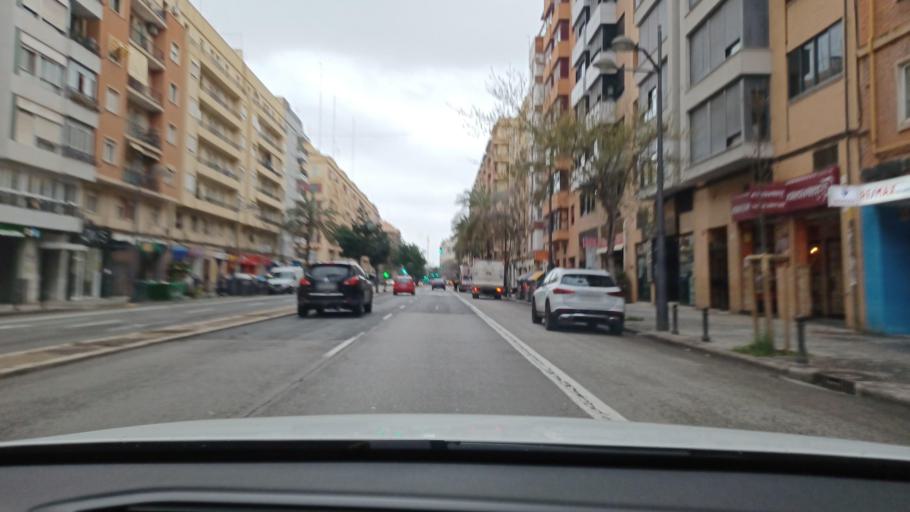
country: ES
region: Valencia
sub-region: Provincia de Valencia
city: Valencia
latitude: 39.4731
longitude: -0.3535
